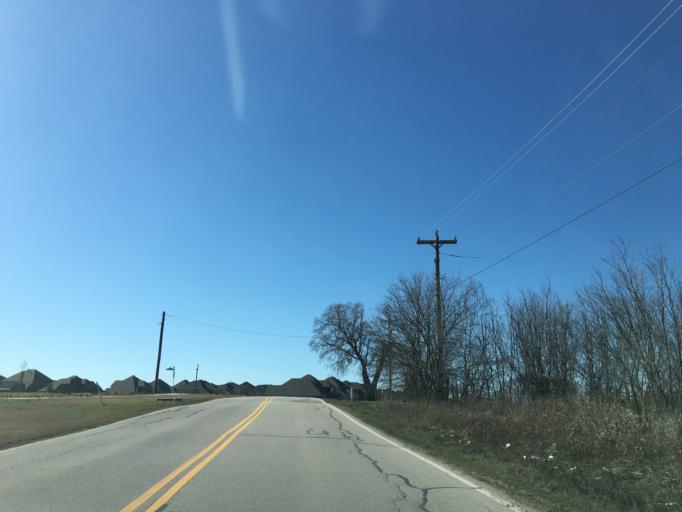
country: US
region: Texas
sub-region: Collin County
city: Prosper
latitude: 33.2305
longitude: -96.8438
